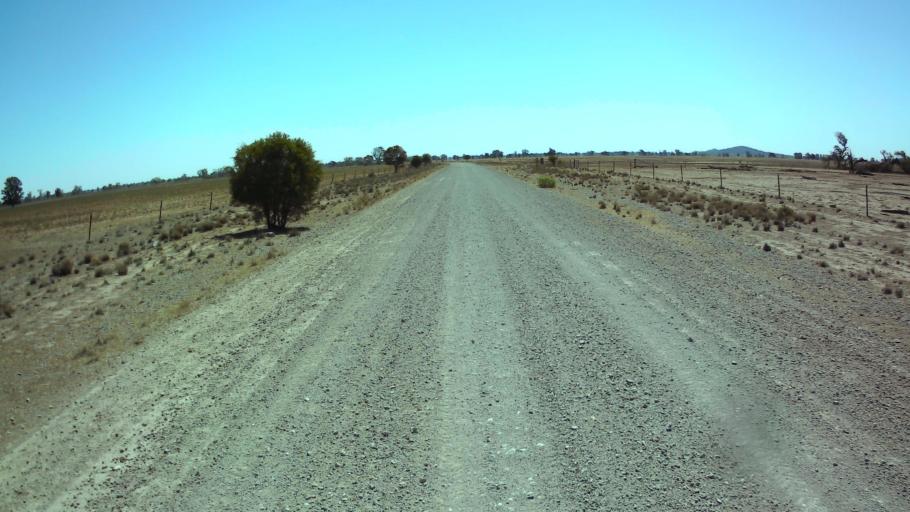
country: AU
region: New South Wales
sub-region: Forbes
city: Forbes
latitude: -33.7456
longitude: 147.7347
